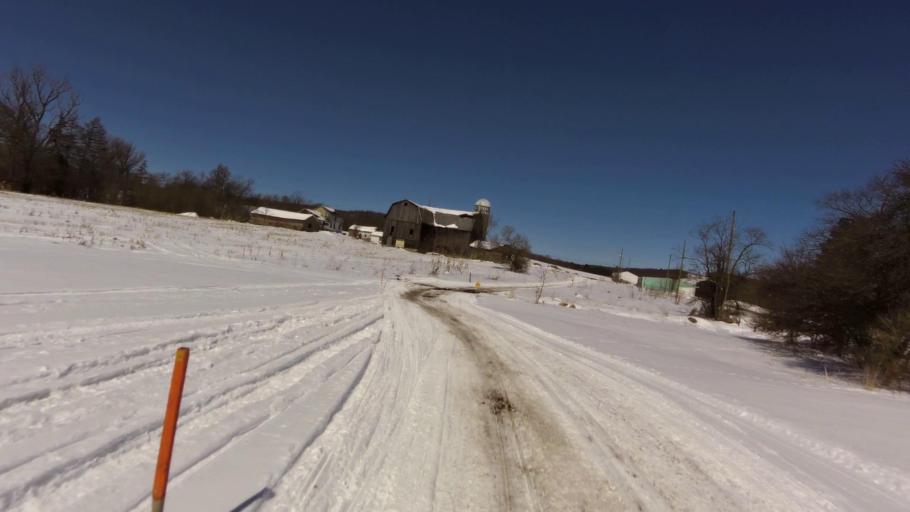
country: US
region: New York
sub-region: Allegany County
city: Houghton
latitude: 42.3907
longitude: -78.2586
